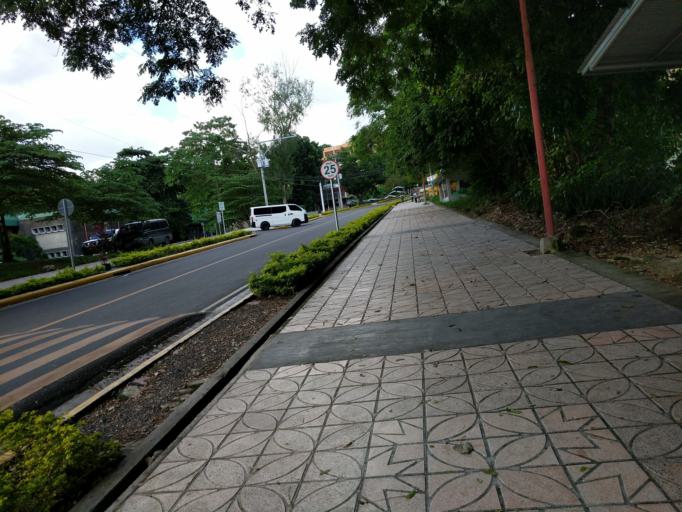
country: PH
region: Central Visayas
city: Mandaue City
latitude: 10.3543
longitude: 123.9126
